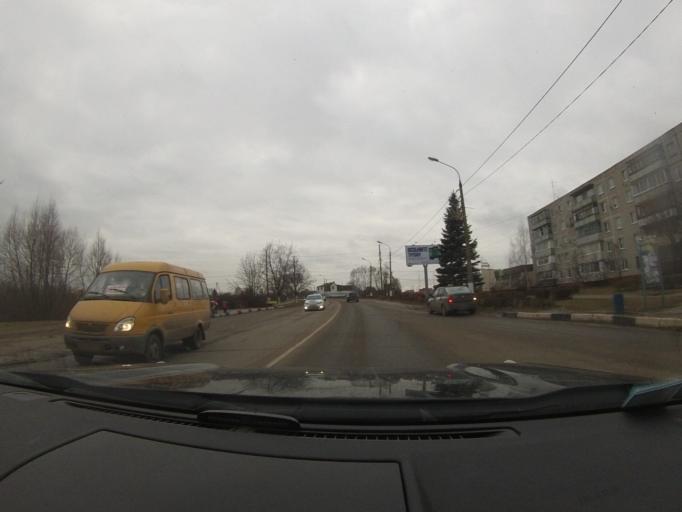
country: RU
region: Moskovskaya
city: Lopatinskiy
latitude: 55.3349
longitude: 38.7122
